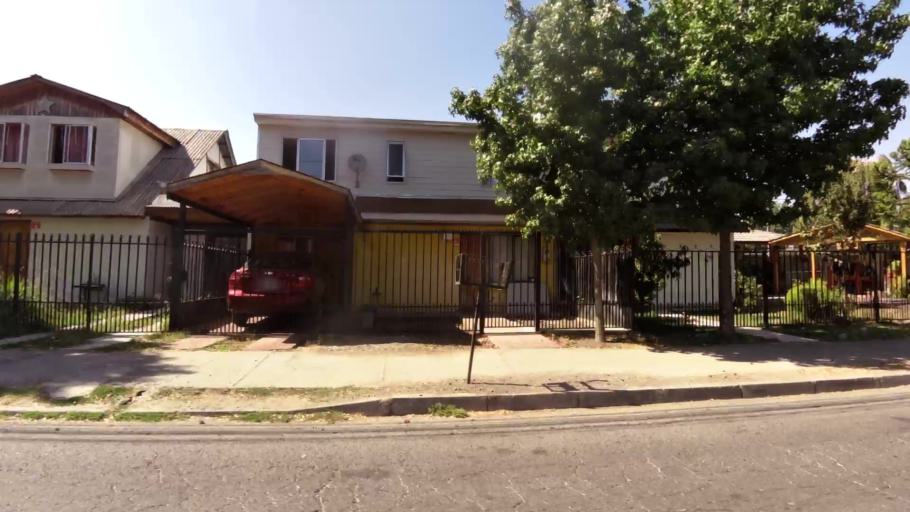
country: CL
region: Maule
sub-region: Provincia de Talca
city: Talca
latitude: -35.4115
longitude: -71.6377
